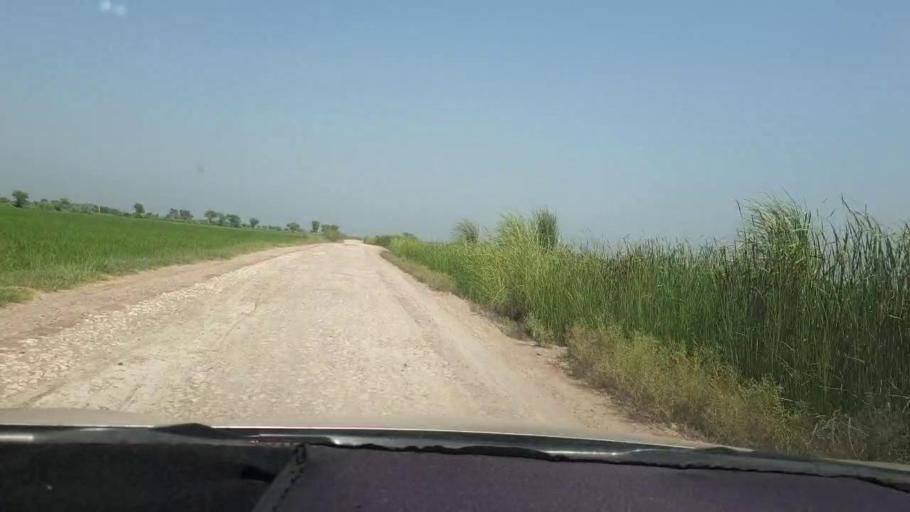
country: PK
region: Sindh
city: Shahdadkot
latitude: 27.8291
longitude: 67.9892
